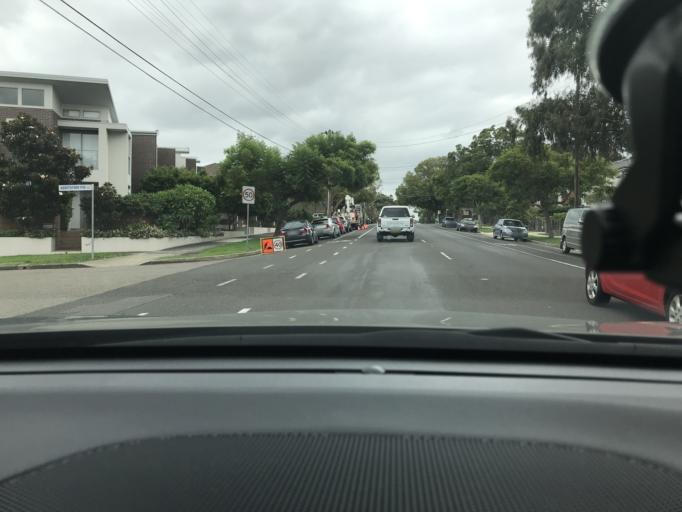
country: AU
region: New South Wales
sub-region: Canada Bay
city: Wareemba
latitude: -33.8492
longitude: 151.1282
